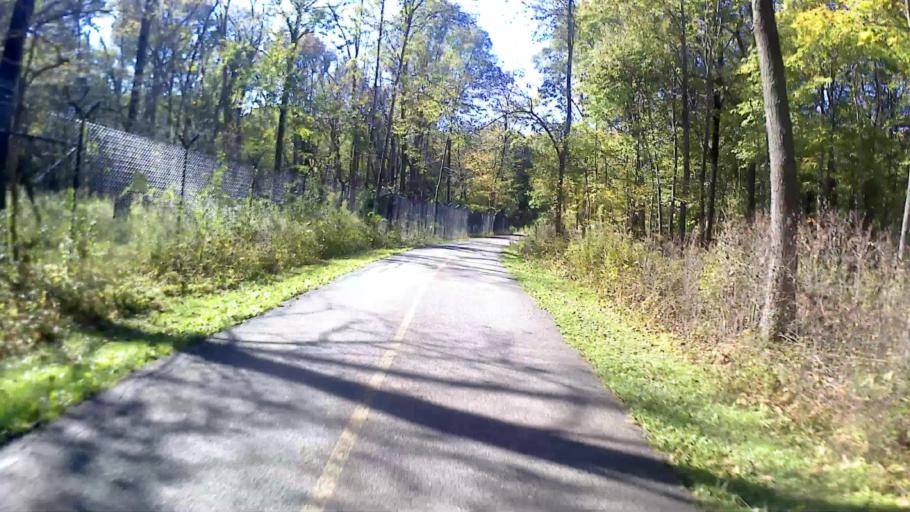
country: US
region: Illinois
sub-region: Cook County
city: Elk Grove Village
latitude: 42.0322
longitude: -87.9890
